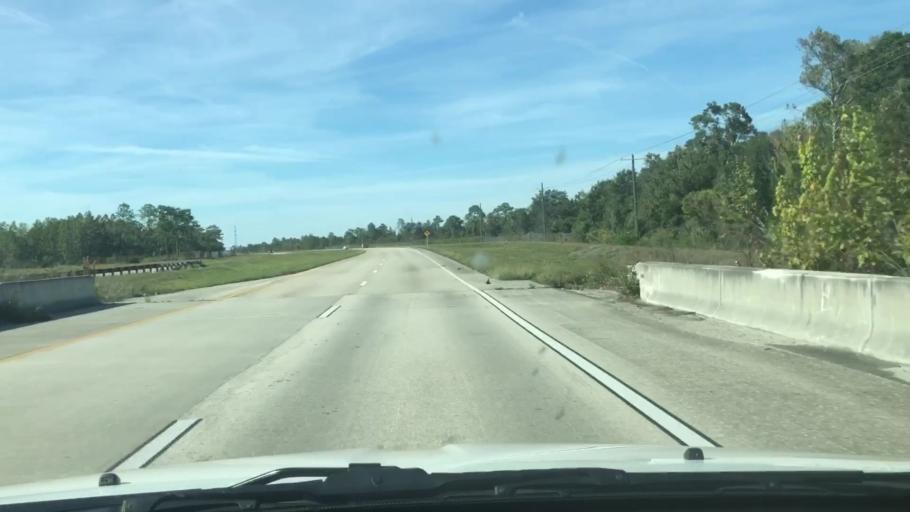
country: US
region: Florida
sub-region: Indian River County
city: Fellsmere
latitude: 27.6887
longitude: -80.8805
